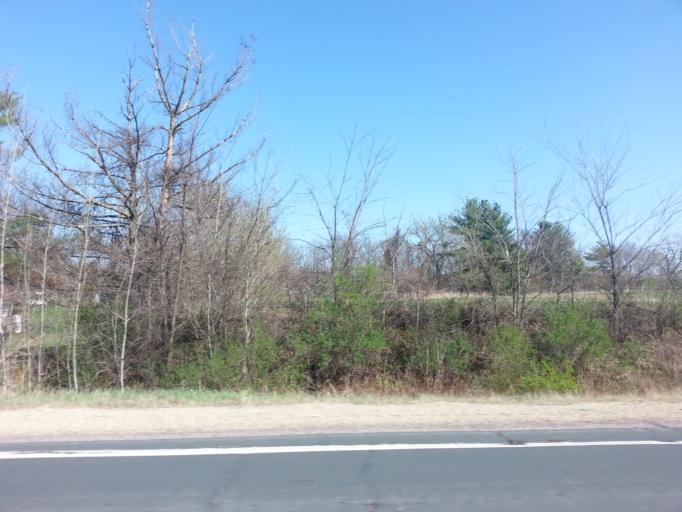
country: US
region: Wisconsin
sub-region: Dunn County
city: Menomonie
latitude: 44.7721
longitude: -91.9373
